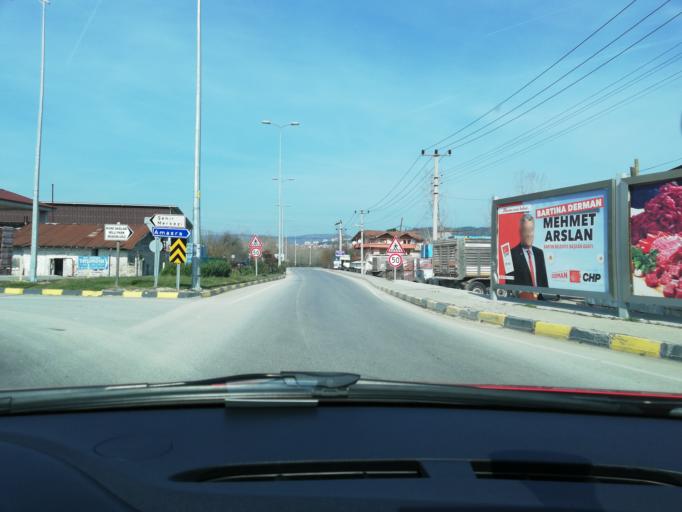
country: TR
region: Bartin
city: Bartin
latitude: 41.6311
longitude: 32.3502
